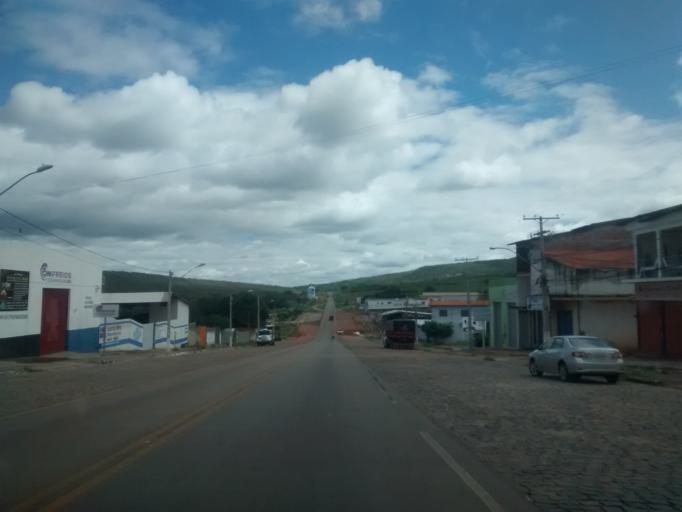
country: BR
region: Bahia
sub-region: Brumado
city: Brumado
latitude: -14.2177
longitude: -41.6846
